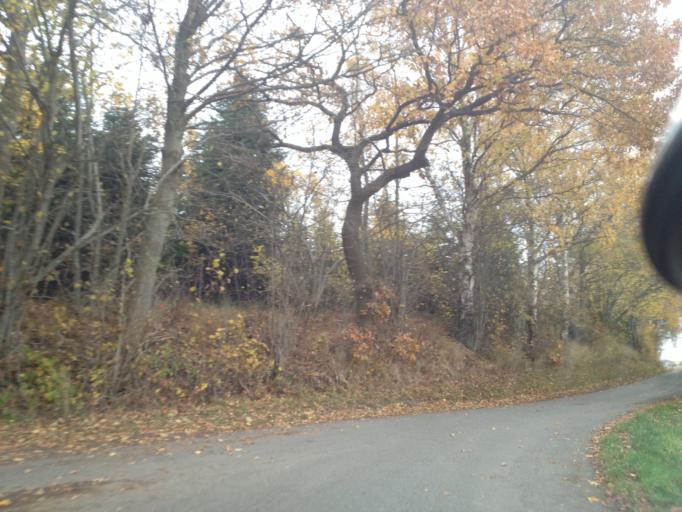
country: DK
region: South Denmark
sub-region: Assens Kommune
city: Vissenbjerg
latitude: 55.4207
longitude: 10.1607
